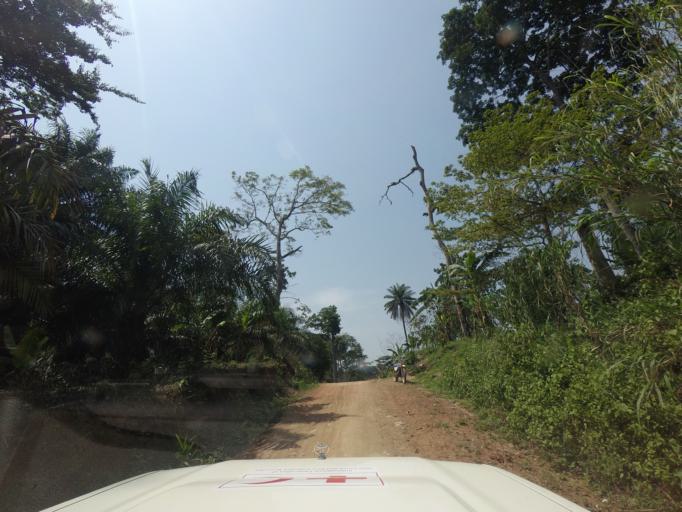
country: LR
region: Lofa
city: Voinjama
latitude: 8.4809
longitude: -9.6629
